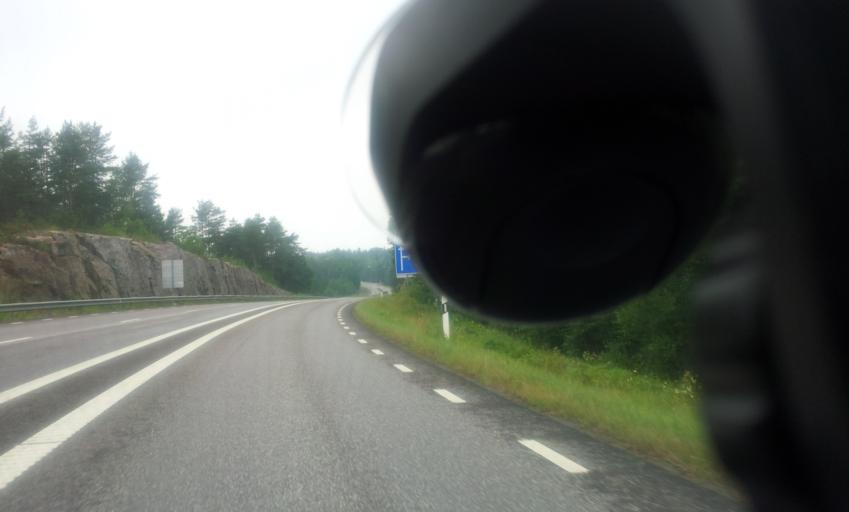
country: SE
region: Kalmar
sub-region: Vasterviks Kommun
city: Ankarsrum
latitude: 57.7214
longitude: 16.4613
